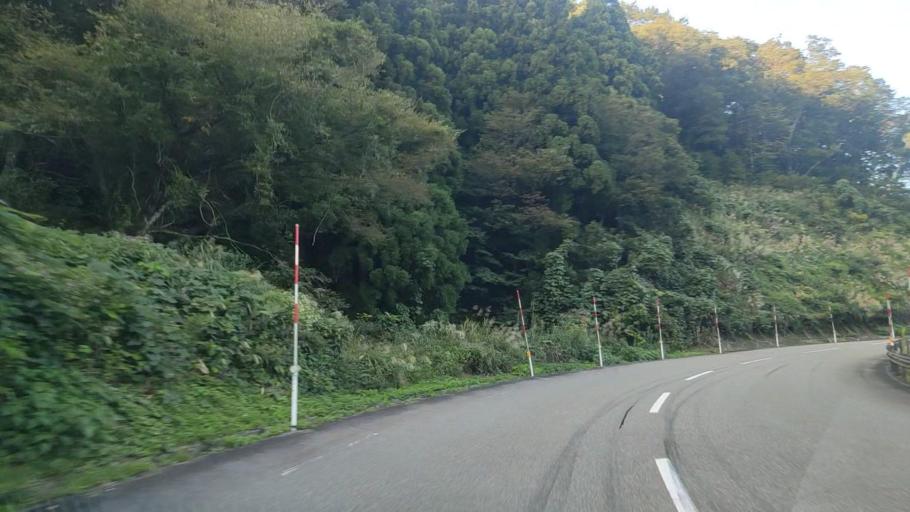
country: JP
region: Toyama
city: Yatsuomachi-higashikumisaka
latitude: 36.5060
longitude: 137.0618
